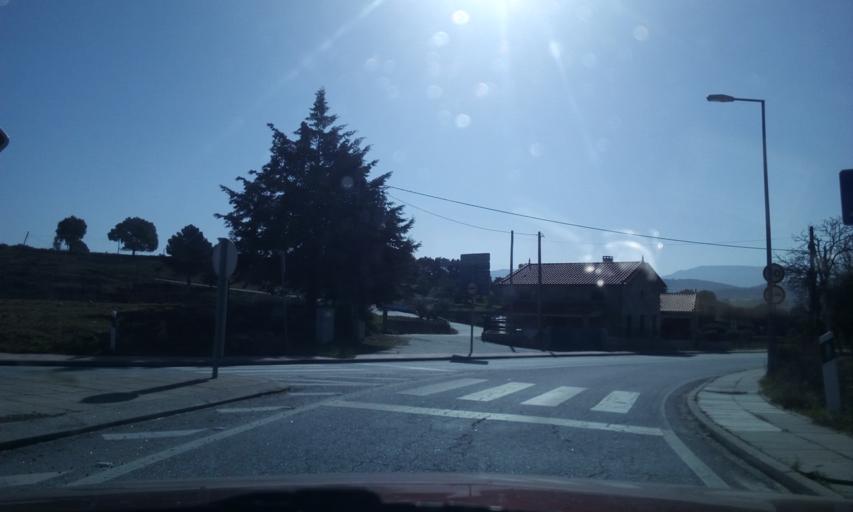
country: PT
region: Guarda
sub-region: Celorico da Beira
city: Celorico da Beira
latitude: 40.6578
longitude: -7.3812
